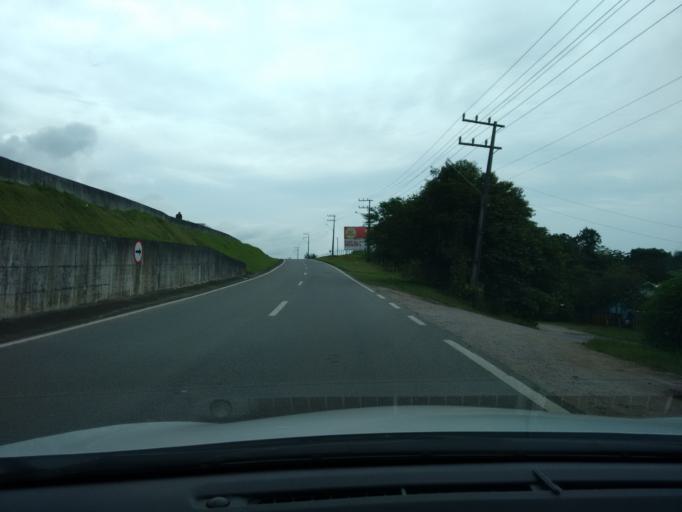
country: BR
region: Santa Catarina
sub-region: Penha
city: Penha
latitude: -26.7605
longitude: -48.6867
